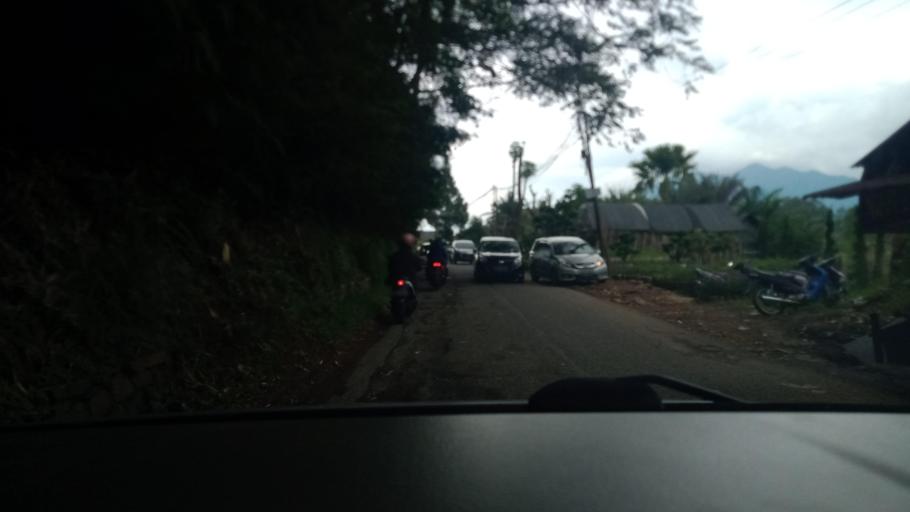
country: ID
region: West Java
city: Lembang
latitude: -6.8209
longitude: 107.5965
